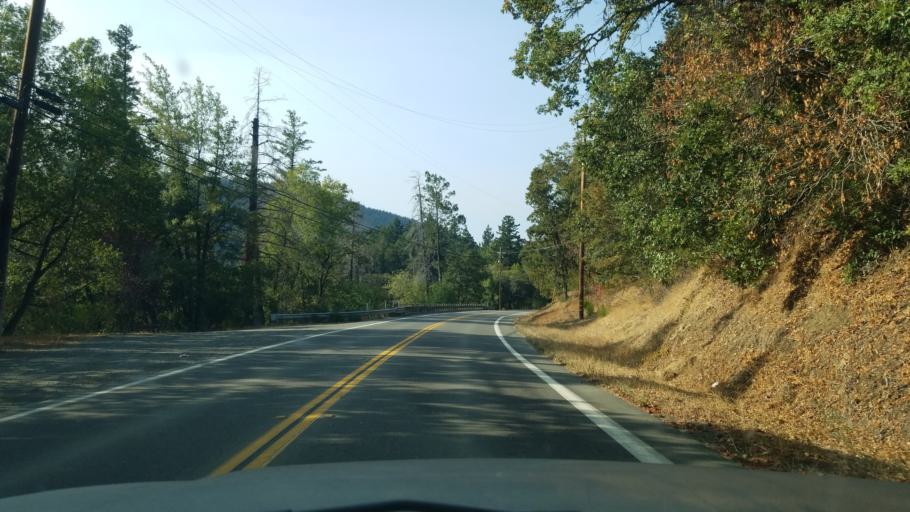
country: US
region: California
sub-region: Humboldt County
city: Redway
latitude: 40.2280
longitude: -123.8232
